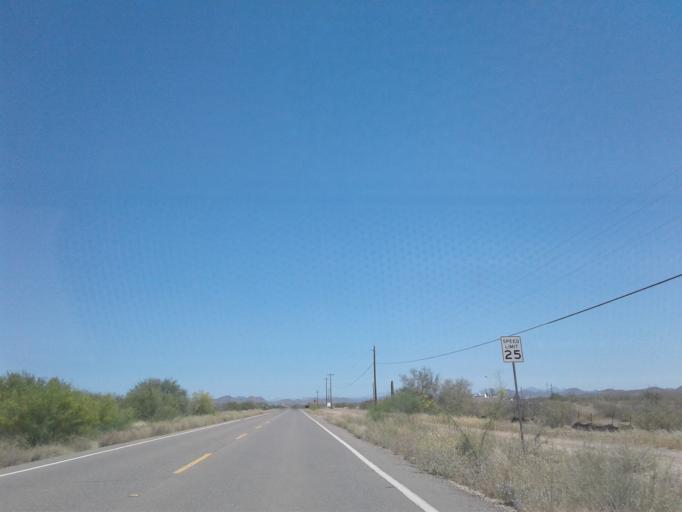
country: US
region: Arizona
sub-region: Maricopa County
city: Anthem
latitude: 33.7979
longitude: -112.2468
